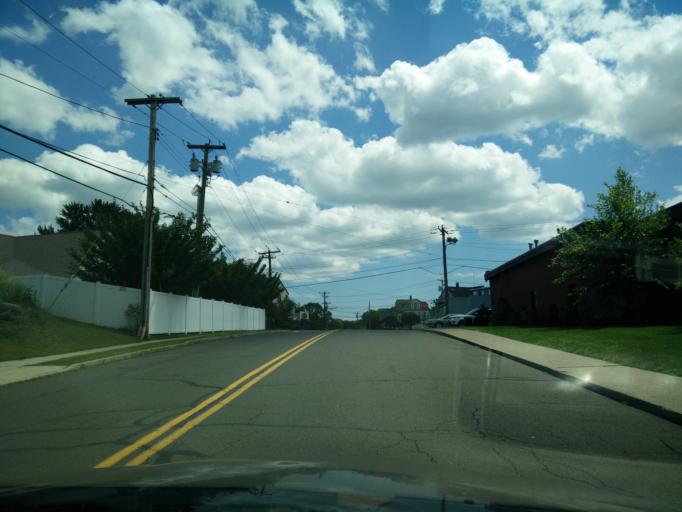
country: US
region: Connecticut
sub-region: Fairfield County
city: Bridgeport
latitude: 41.1777
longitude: -73.2266
